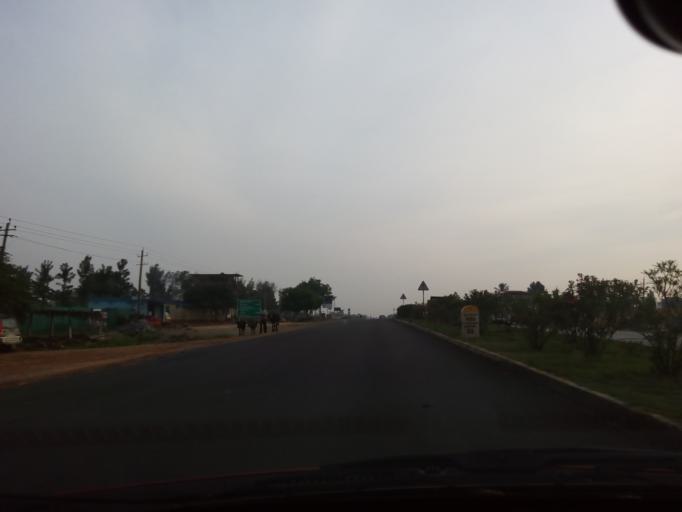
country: IN
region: Karnataka
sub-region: Chikkaballapur
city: Gudibanda
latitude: 13.5751
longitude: 77.7811
